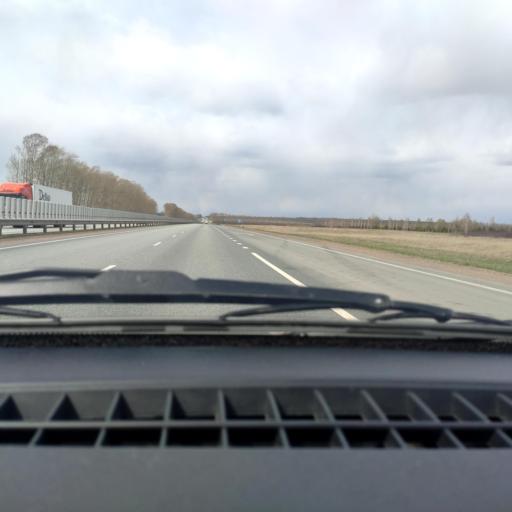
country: RU
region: Bashkortostan
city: Asanovo
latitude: 55.0045
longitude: 55.4912
